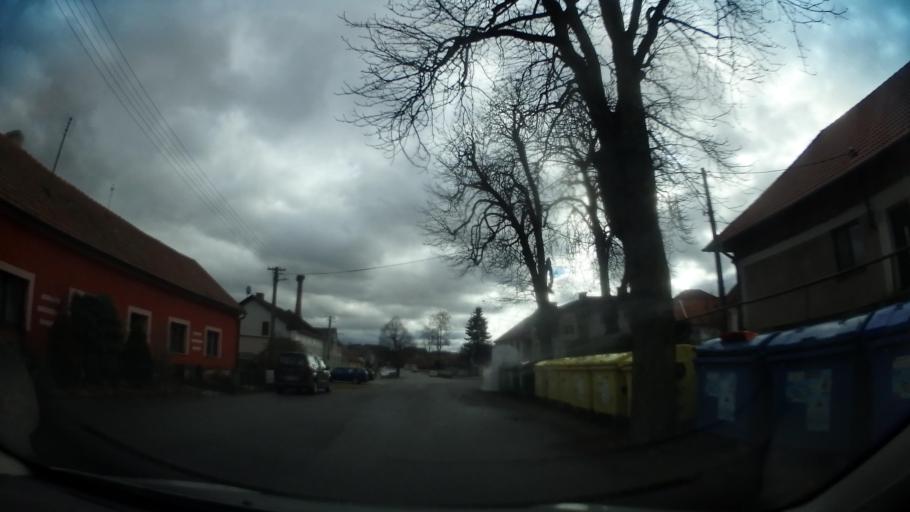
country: CZ
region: Vysocina
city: Budisov
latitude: 49.2887
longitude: 16.0946
